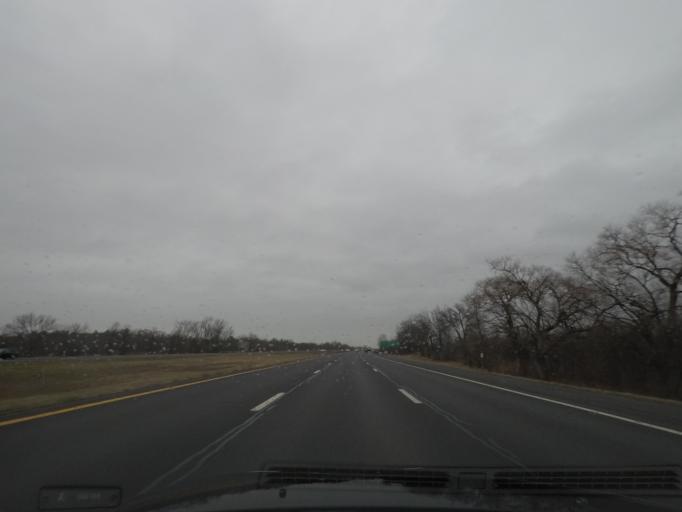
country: US
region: New York
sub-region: Rensselaer County
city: Hampton Manor
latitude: 42.6368
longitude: -73.7076
